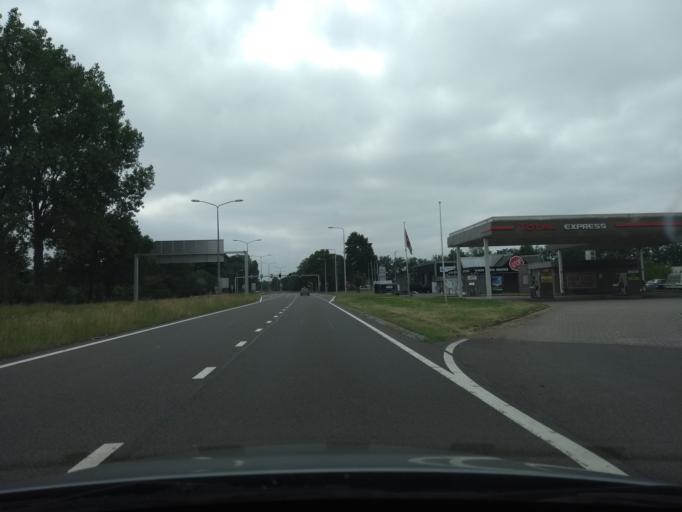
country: NL
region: Overijssel
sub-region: Gemeente Wierden
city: Wierden
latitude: 52.3531
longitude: 6.6244
